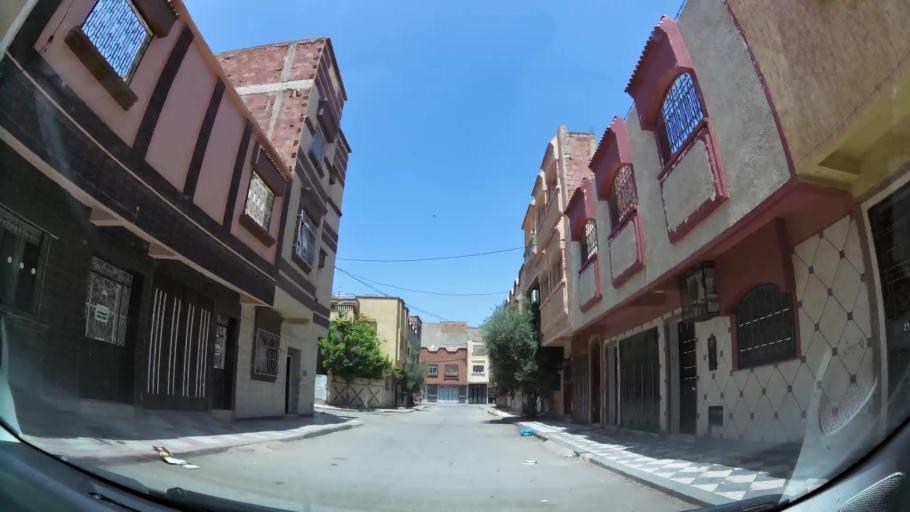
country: MA
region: Oriental
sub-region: Oujda-Angad
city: Oujda
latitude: 34.6905
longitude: -1.8880
